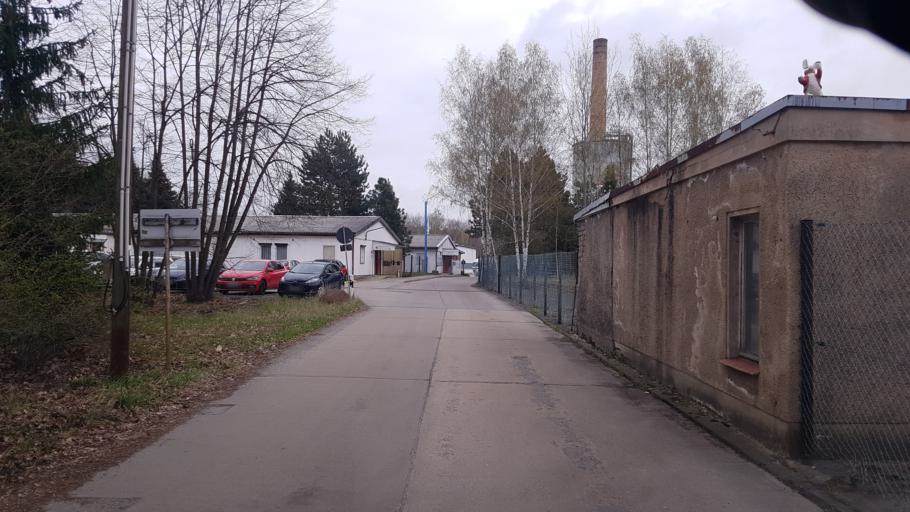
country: DE
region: Brandenburg
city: Lauchhammer
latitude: 51.4926
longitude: 13.7874
